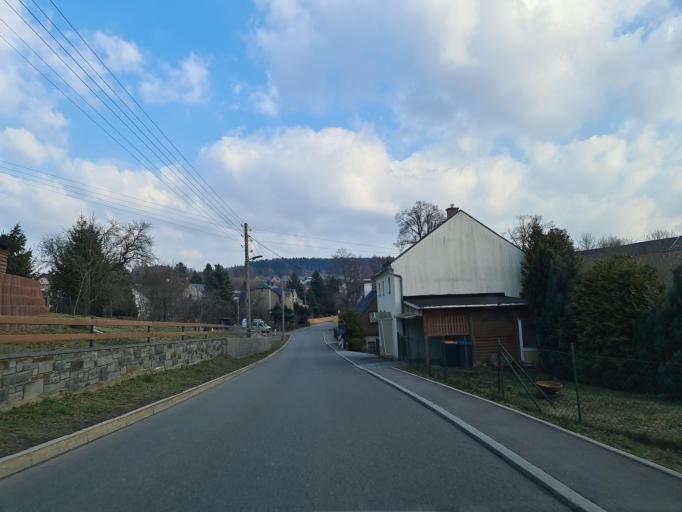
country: DE
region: Saxony
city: Rodewisch
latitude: 50.5216
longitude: 12.4266
